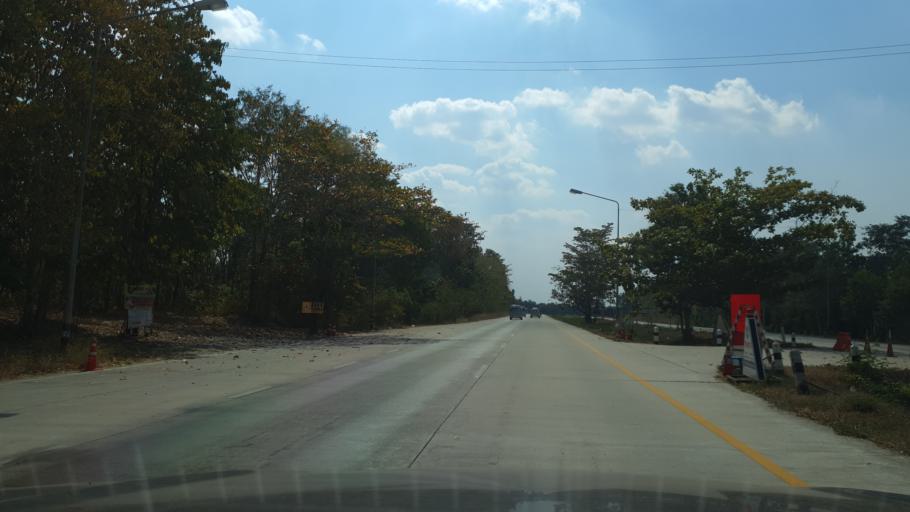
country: TH
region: Lampang
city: Mae Phrik
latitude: 17.3100
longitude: 99.1490
